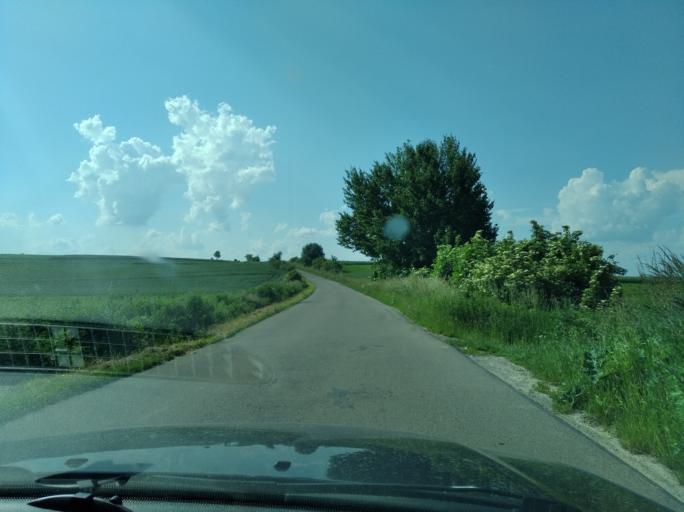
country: PL
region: Subcarpathian Voivodeship
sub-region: Powiat jaroslawski
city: Rokietnica
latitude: 49.9322
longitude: 22.6736
